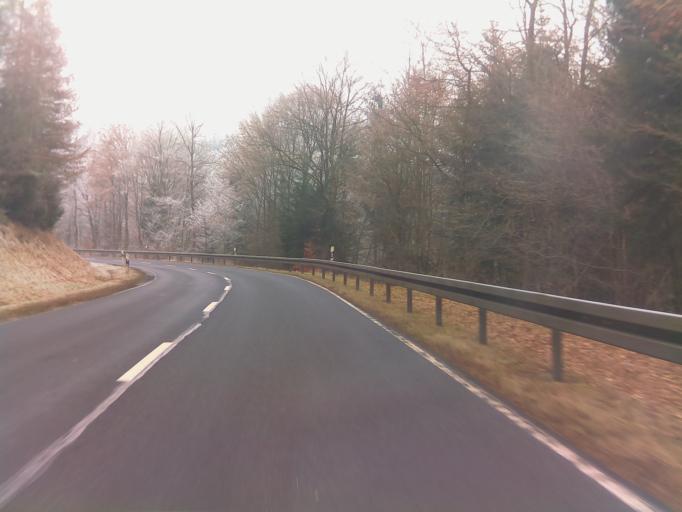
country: DE
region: Bavaria
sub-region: Regierungsbezirk Unterfranken
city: Obersinn
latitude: 50.2539
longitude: 9.5624
